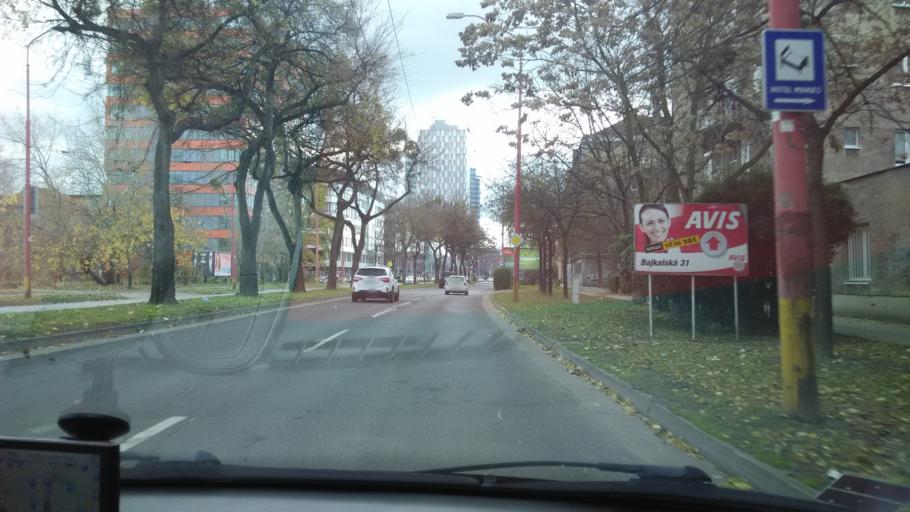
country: SK
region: Bratislavsky
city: Bratislava
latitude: 48.1522
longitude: 17.1257
